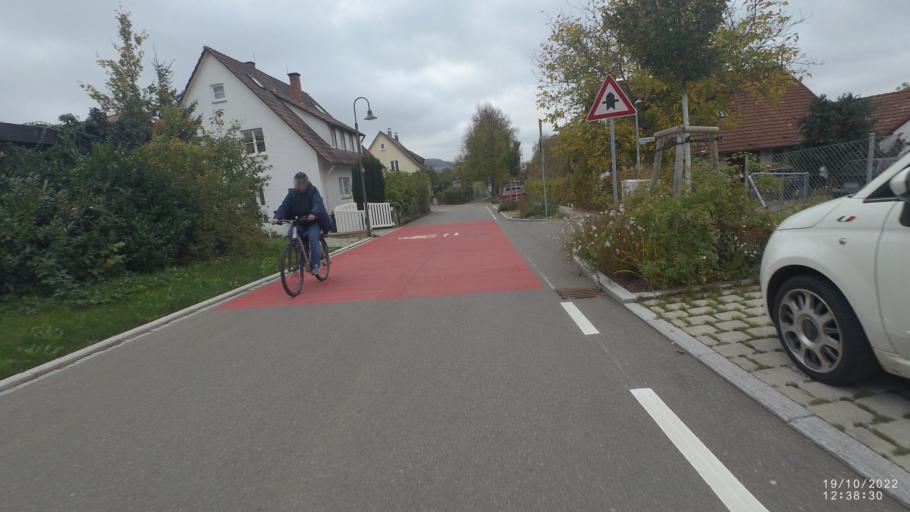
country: DE
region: Baden-Wuerttemberg
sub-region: Regierungsbezirk Stuttgart
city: Boll
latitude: 48.6394
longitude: 9.6123
